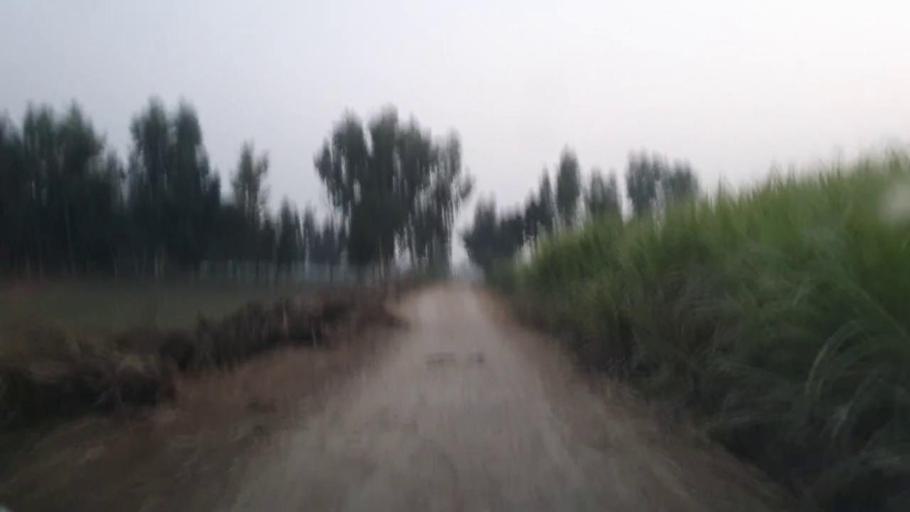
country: PK
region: Sindh
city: Karaundi
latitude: 26.9279
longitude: 68.4299
